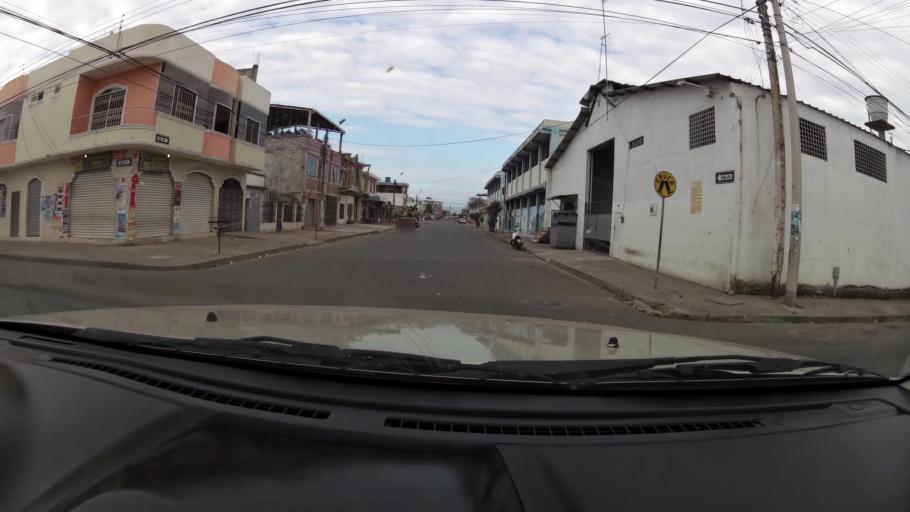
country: EC
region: El Oro
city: Machala
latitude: -3.2506
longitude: -79.9511
